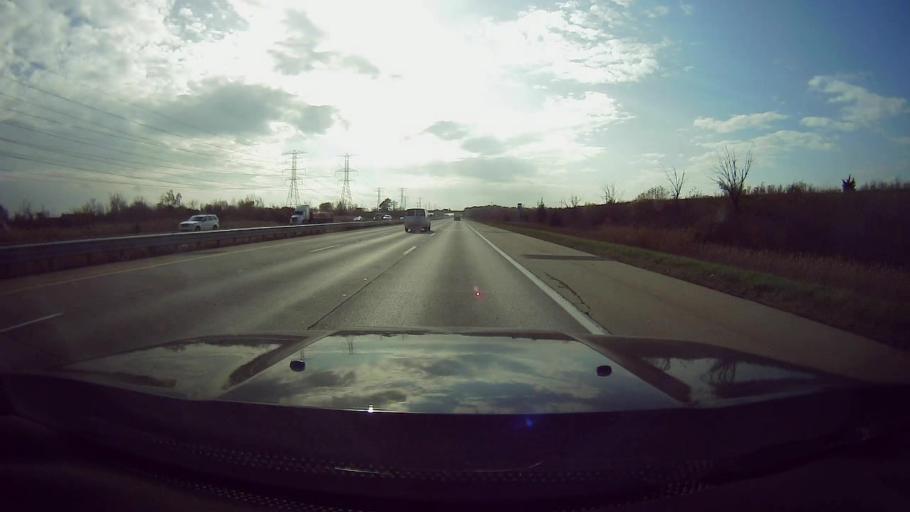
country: US
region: Michigan
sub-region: Monroe County
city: South Rockwood
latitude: 42.0552
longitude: -83.2661
